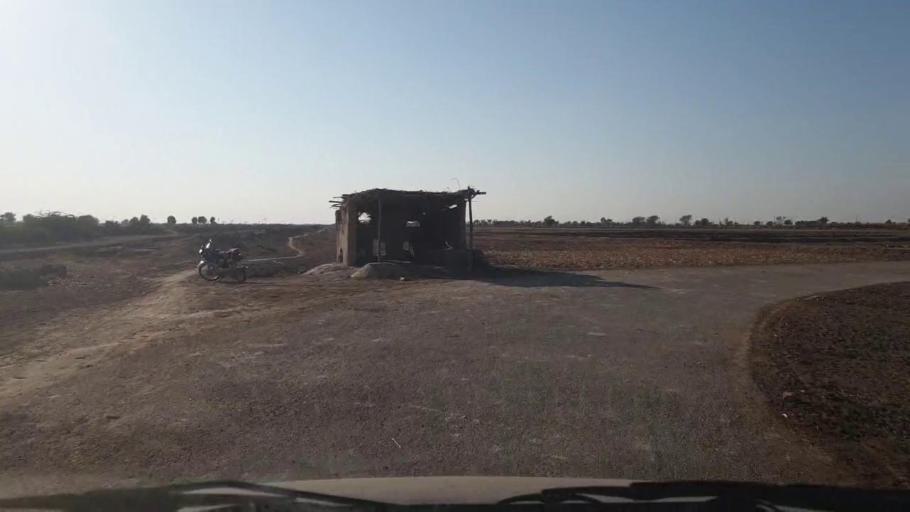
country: PK
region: Sindh
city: Samaro
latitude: 25.3522
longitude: 69.2871
